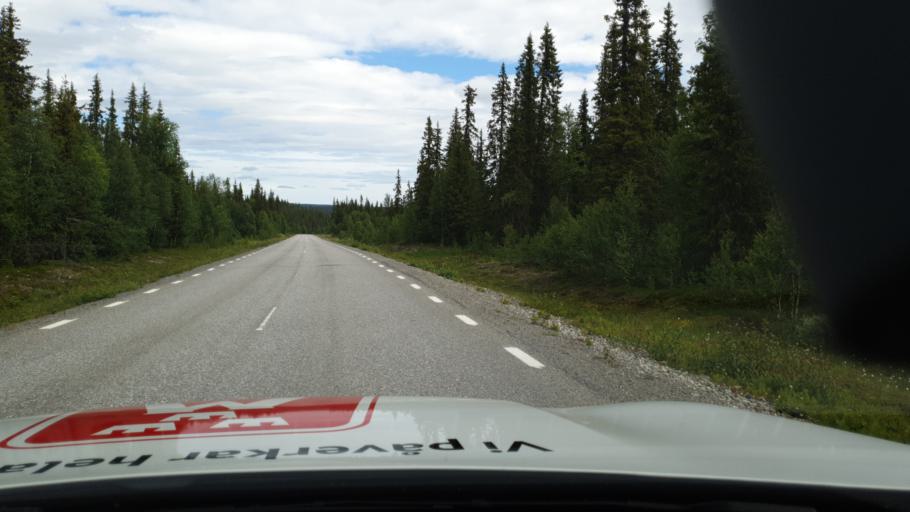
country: SE
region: Vaesterbotten
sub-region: Storumans Kommun
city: Fristad
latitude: 65.4478
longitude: 16.7409
